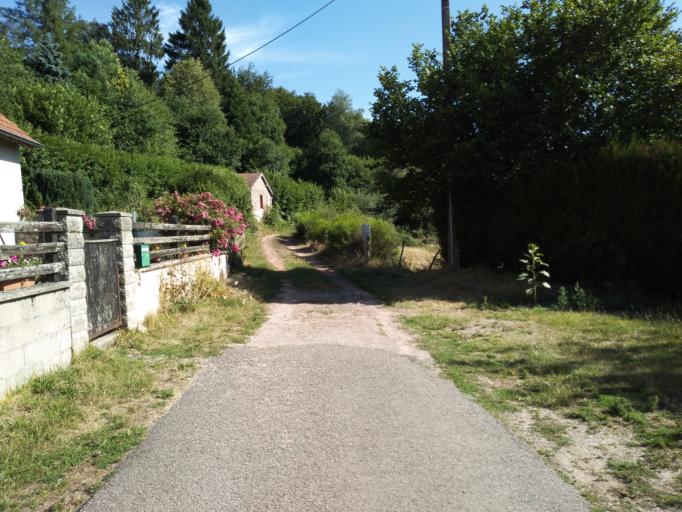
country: FR
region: Bourgogne
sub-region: Departement de la Cote-d'Or
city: Saulieu
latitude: 47.2930
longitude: 4.1376
